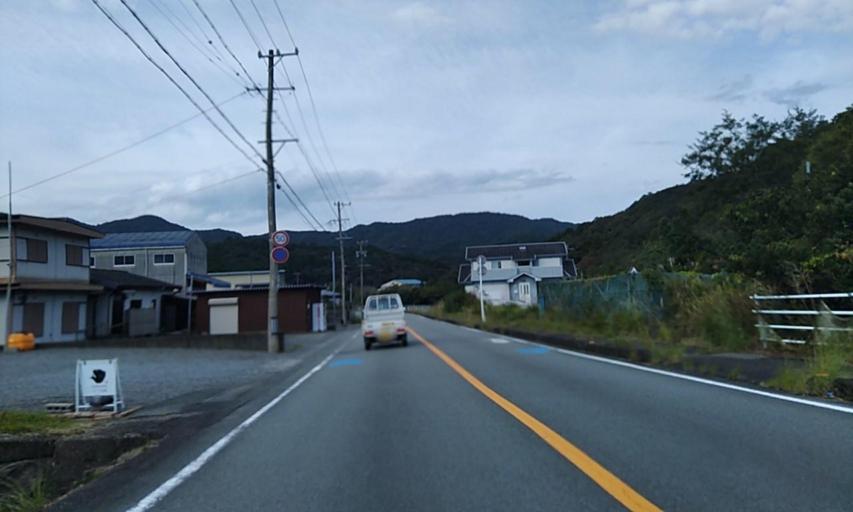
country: JP
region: Mie
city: Ise
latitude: 34.3034
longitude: 136.6370
